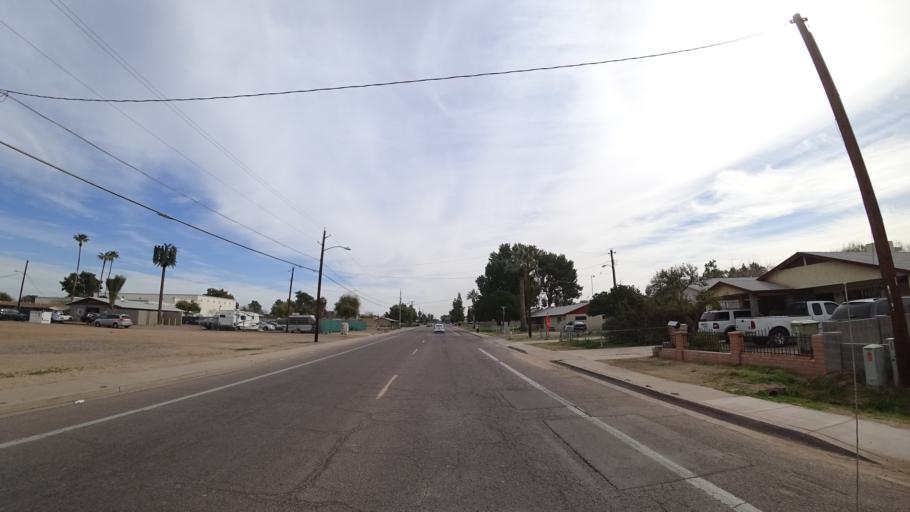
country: US
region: Arizona
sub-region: Maricopa County
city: Glendale
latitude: 33.5311
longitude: -112.1988
